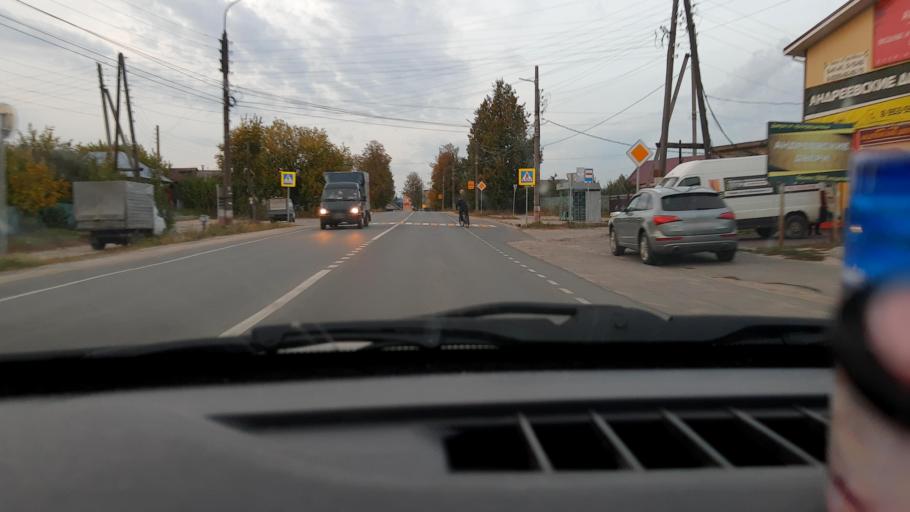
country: RU
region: Nizjnij Novgorod
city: Gorodets
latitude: 56.6614
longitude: 43.4696
